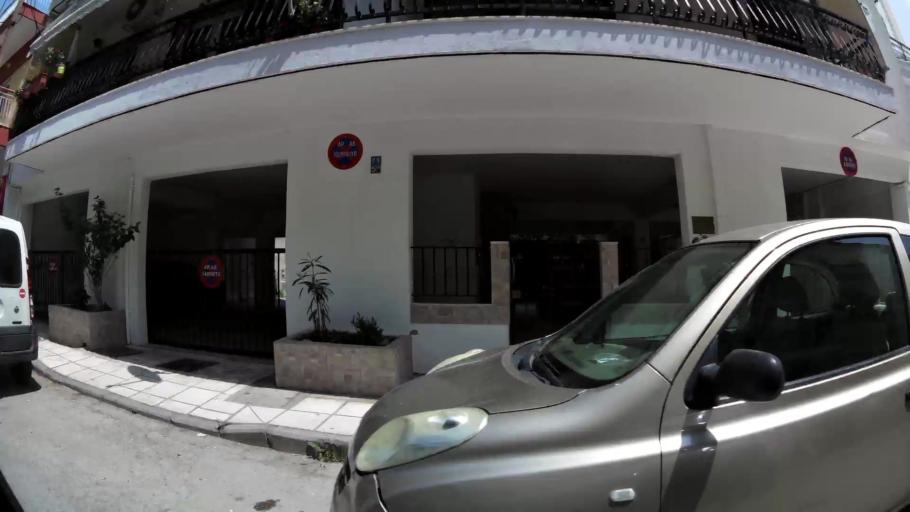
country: GR
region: Central Macedonia
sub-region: Nomos Thessalonikis
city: Evosmos
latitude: 40.6701
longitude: 22.9099
